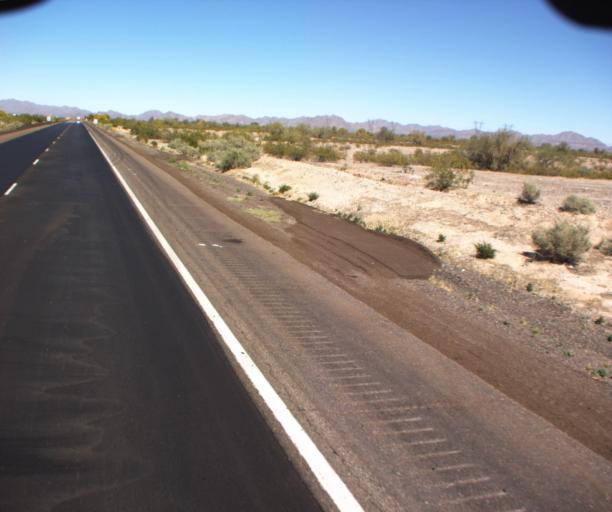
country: US
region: Arizona
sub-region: Maricopa County
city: Gila Bend
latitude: 32.9837
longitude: -112.6668
